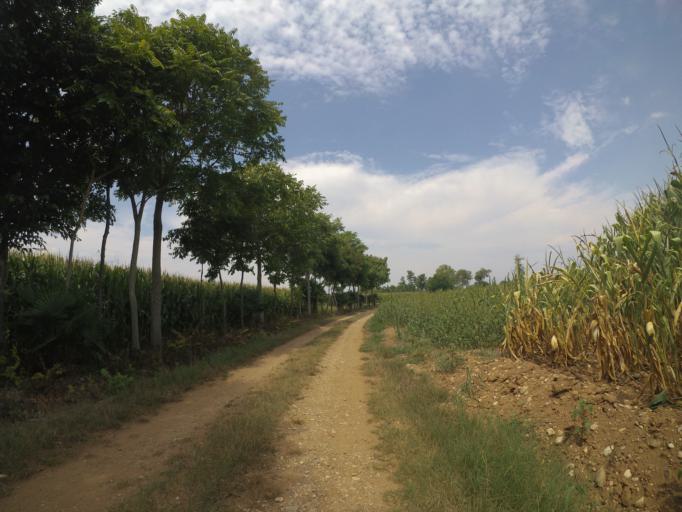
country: IT
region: Friuli Venezia Giulia
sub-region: Provincia di Udine
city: Bertiolo
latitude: 45.9590
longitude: 13.0692
